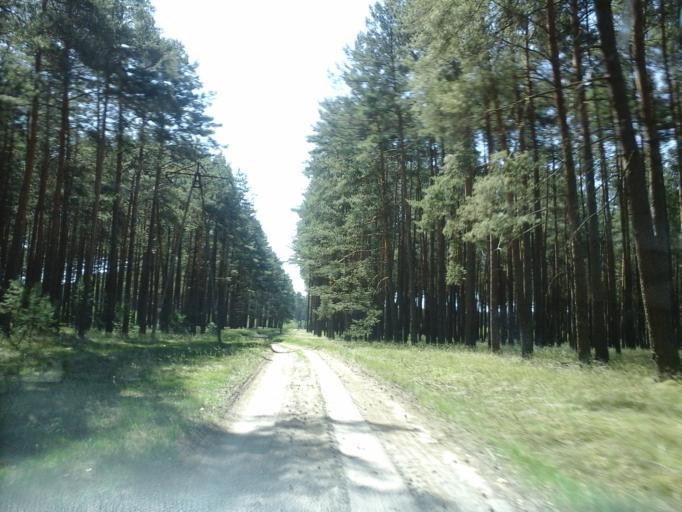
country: PL
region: West Pomeranian Voivodeship
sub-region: Powiat drawski
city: Kalisz Pomorski
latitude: 53.1684
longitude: 15.9789
